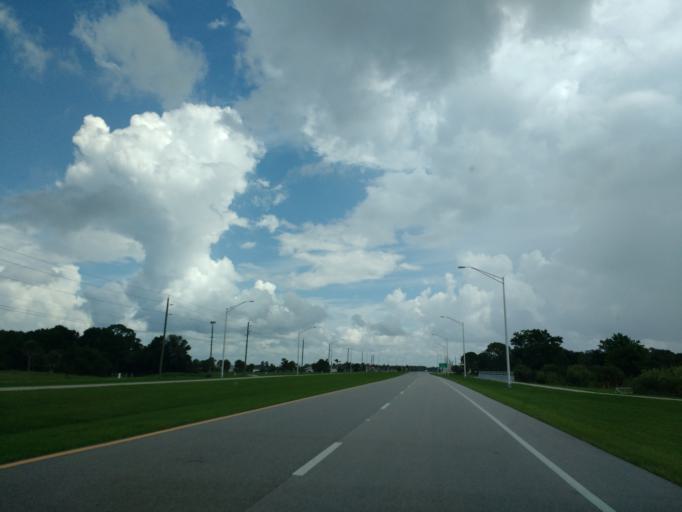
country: US
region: Florida
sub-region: Lee County
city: Burnt Store Marina
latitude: 26.7830
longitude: -82.0379
